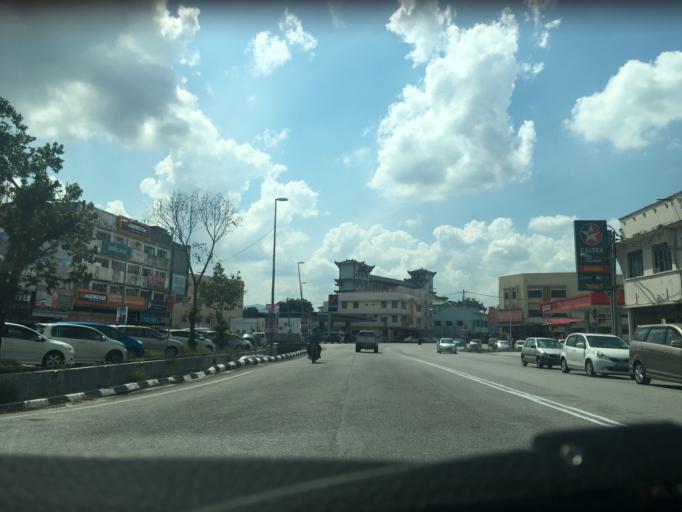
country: MY
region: Perak
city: Ipoh
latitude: 4.5826
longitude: 101.0821
